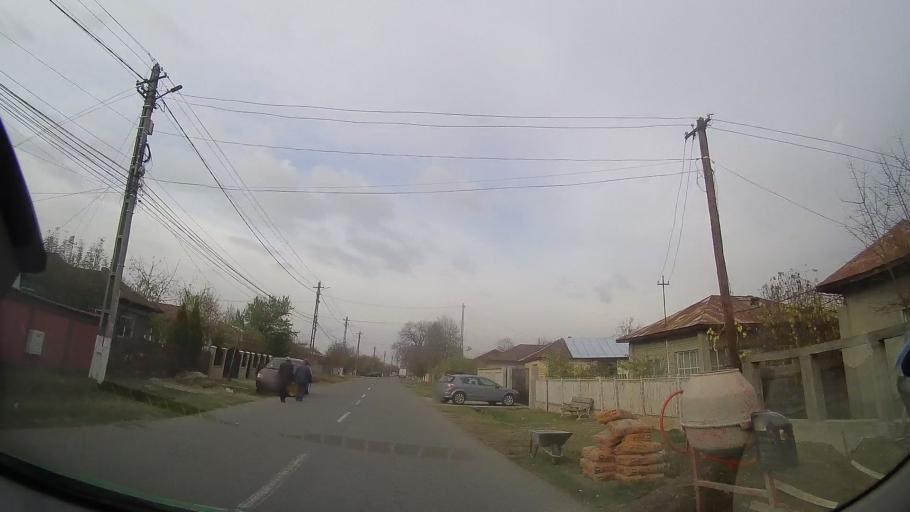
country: RO
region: Prahova
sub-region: Comuna Gorgota
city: Potigrafu
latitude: 44.7786
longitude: 26.1035
